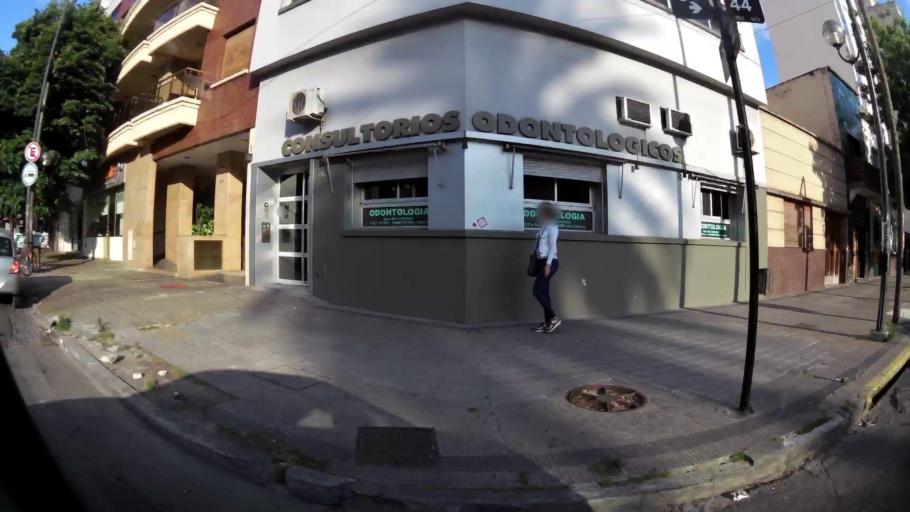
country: AR
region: Buenos Aires
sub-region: Partido de La Plata
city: La Plata
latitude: -34.9158
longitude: -57.9609
